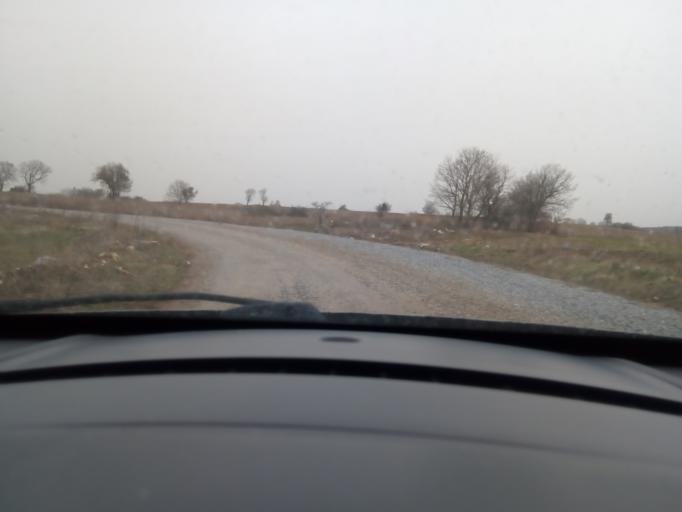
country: TR
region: Balikesir
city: Omerkoy
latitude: 39.8883
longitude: 28.0267
